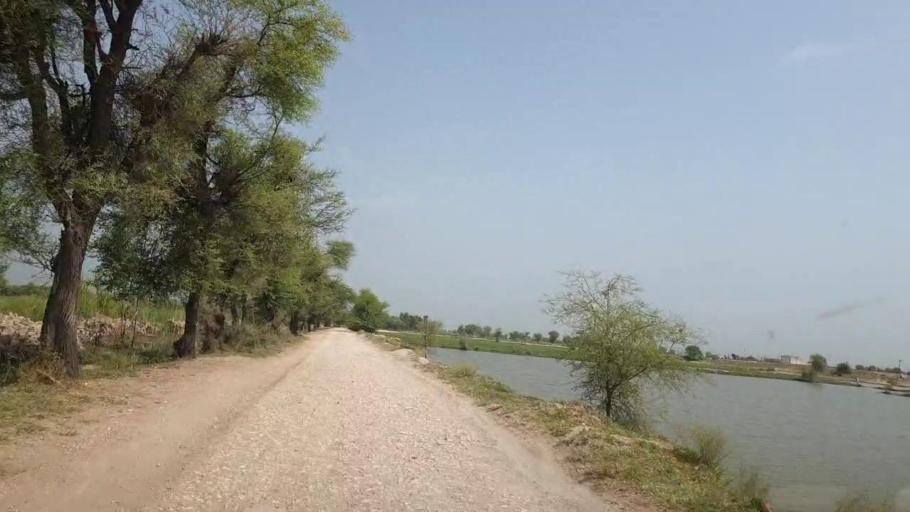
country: PK
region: Sindh
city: Lakhi
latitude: 27.8754
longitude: 68.6587
